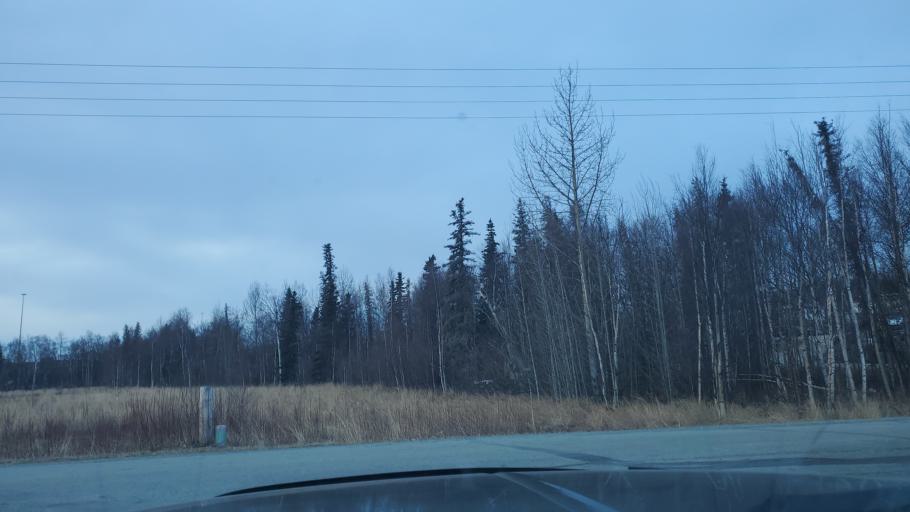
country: US
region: Alaska
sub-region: Matanuska-Susitna Borough
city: Lakes
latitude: 61.5729
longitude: -149.3446
